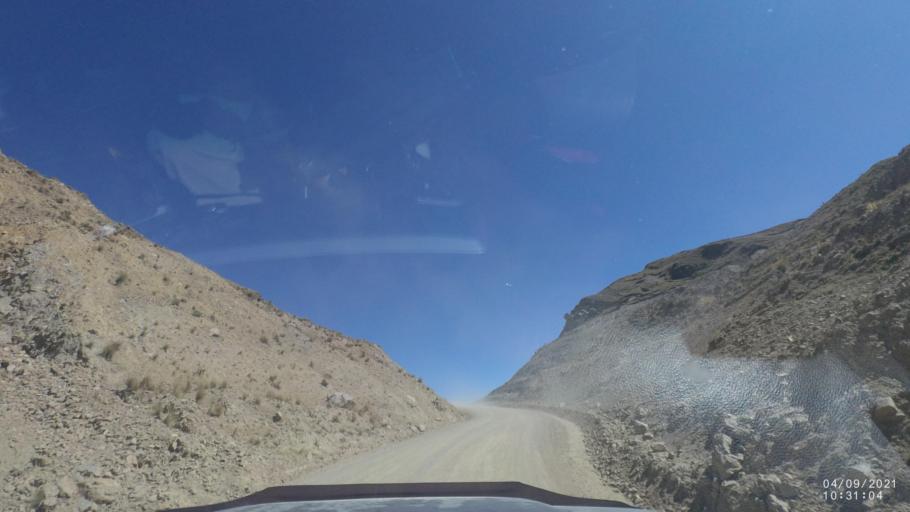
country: BO
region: Cochabamba
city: Sipe Sipe
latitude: -17.3032
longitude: -66.4451
